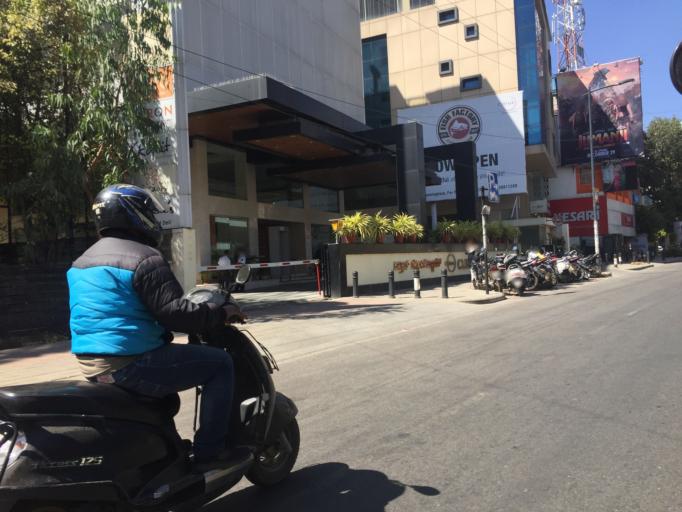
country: IN
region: Karnataka
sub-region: Bangalore Urban
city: Bangalore
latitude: 12.9860
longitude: 77.5957
